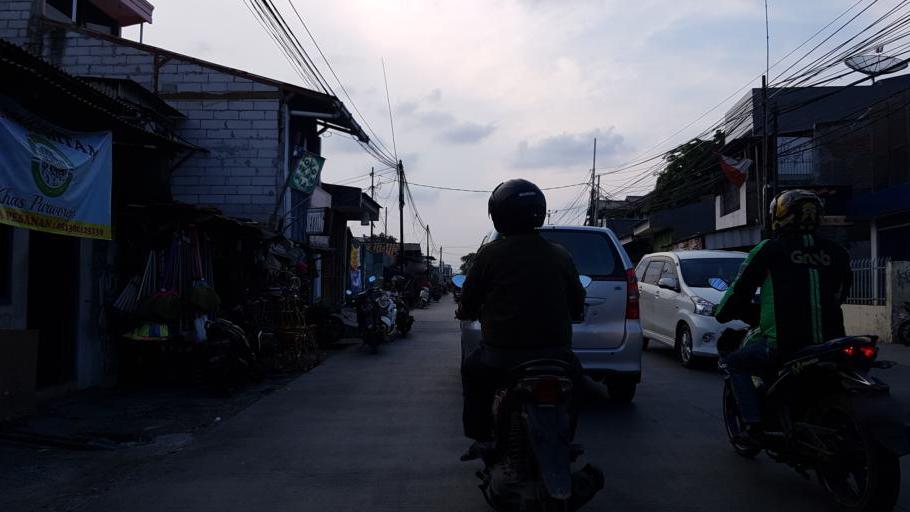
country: ID
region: Jakarta Raya
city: Jakarta
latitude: -6.1375
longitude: 106.7586
